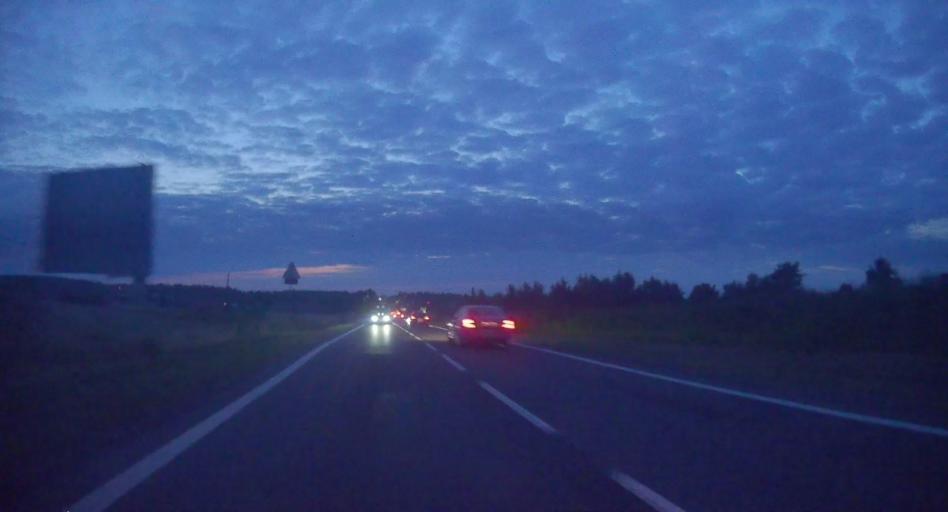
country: PL
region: Silesian Voivodeship
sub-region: Powiat klobucki
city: Kamyk
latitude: 50.8560
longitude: 19.0313
